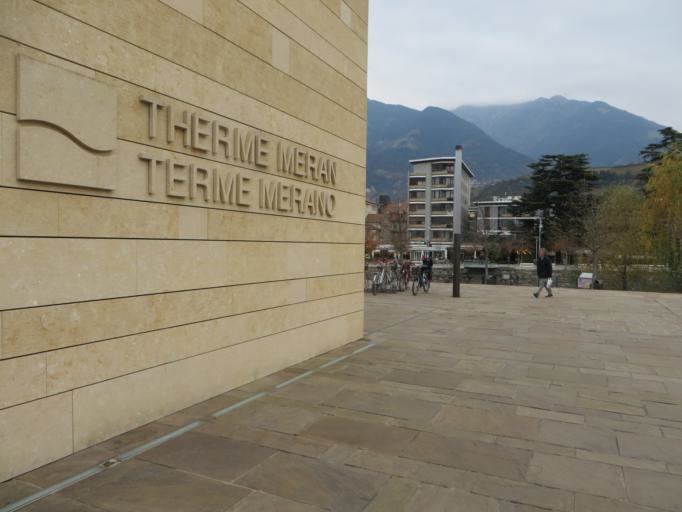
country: IT
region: Trentino-Alto Adige
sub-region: Bolzano
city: Merano
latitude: 46.6694
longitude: 11.1608
